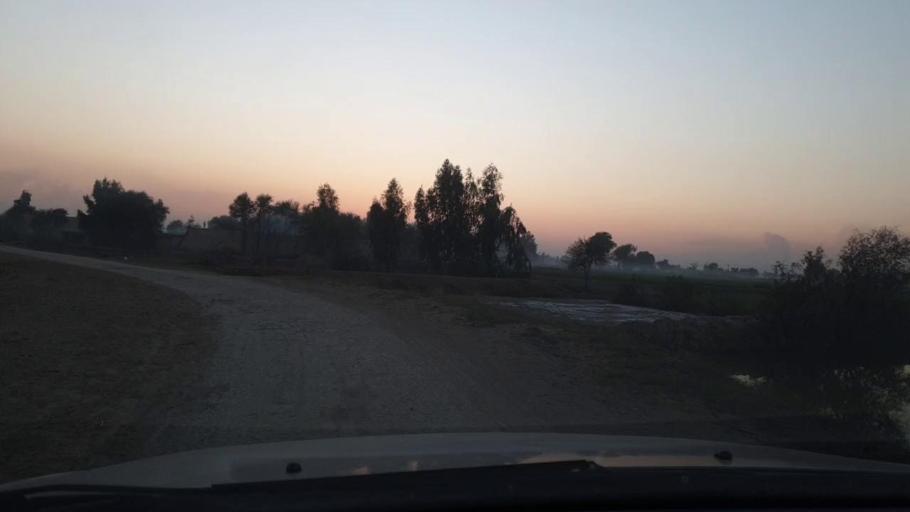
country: PK
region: Sindh
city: Mirpur Mathelo
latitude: 28.0245
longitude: 69.5174
